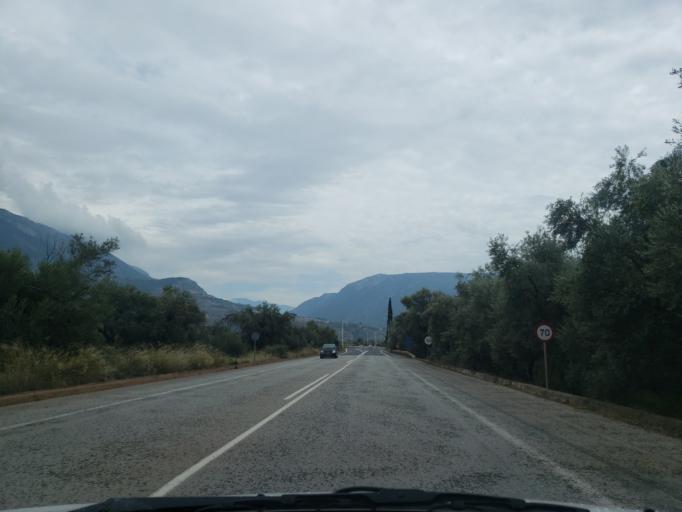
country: GR
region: Central Greece
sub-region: Nomos Fokidos
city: Itea
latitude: 38.4818
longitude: 22.4309
